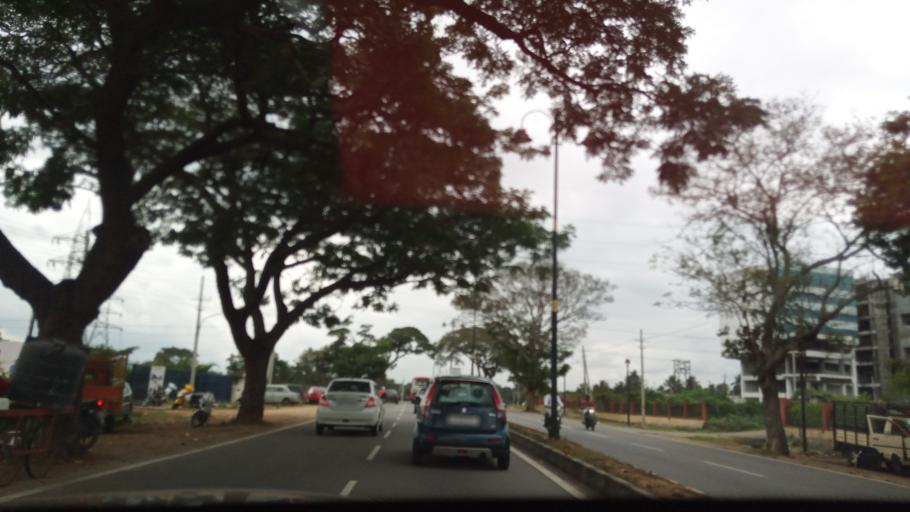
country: IN
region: Karnataka
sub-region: Mysore
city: Mysore
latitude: 12.3464
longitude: 76.6597
